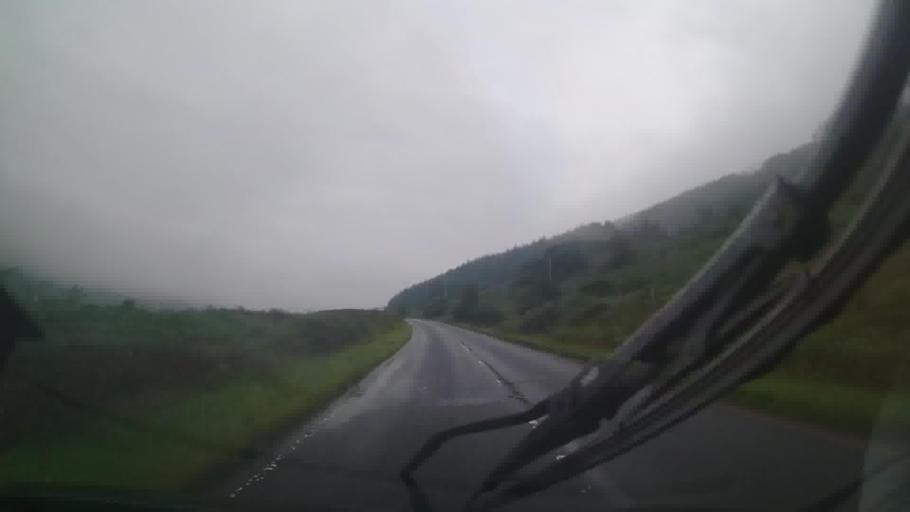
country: GB
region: Scotland
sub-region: Argyll and Bute
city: Oban
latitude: 56.6911
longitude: -5.5225
